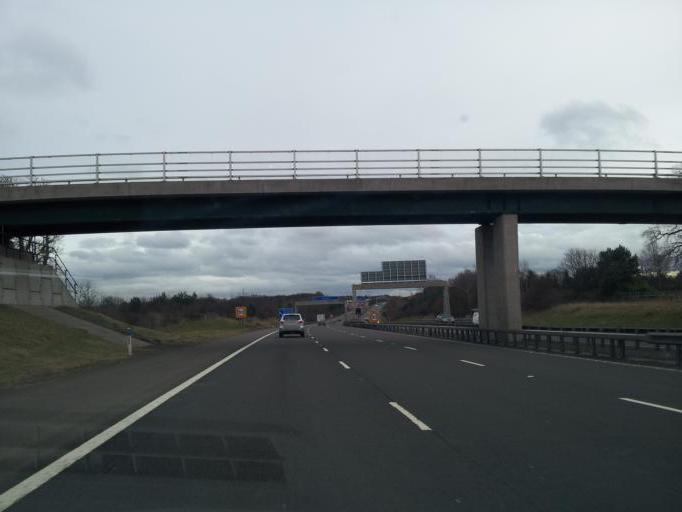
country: GB
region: England
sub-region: Staffordshire
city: Shenstone
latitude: 52.6333
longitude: -1.8054
